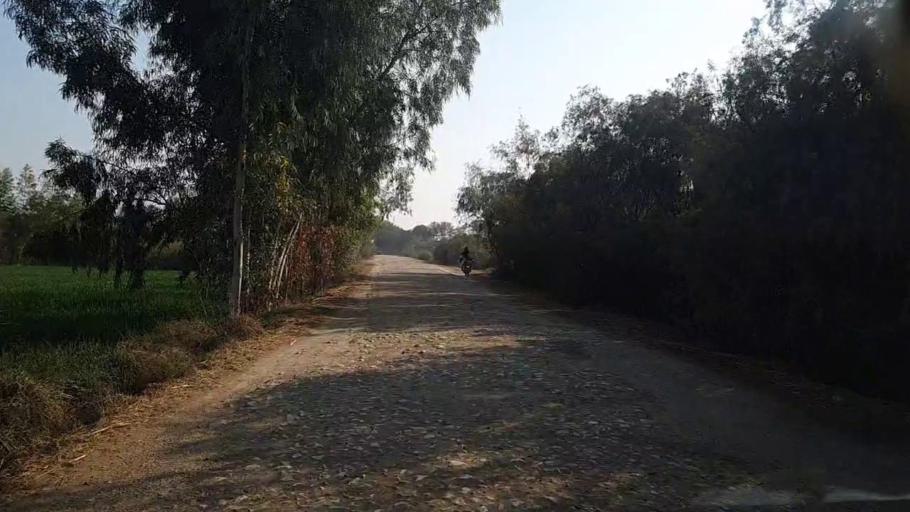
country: PK
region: Sindh
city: Mirpur Mathelo
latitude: 27.8851
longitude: 69.6110
